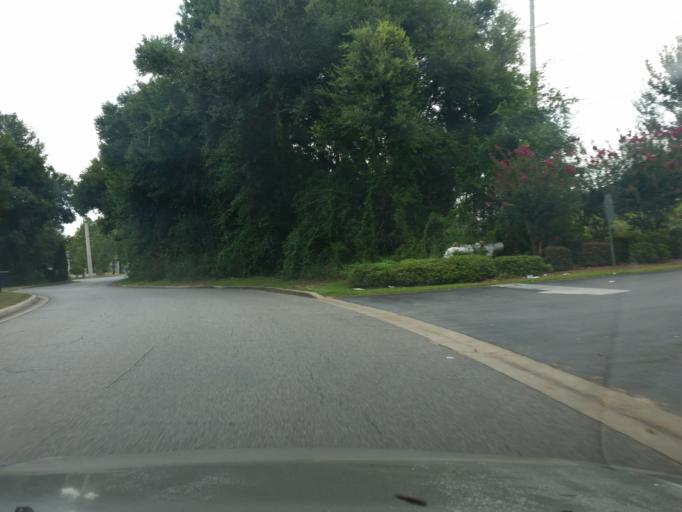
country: US
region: Florida
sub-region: Escambia County
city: Brent
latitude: 30.4788
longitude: -87.2662
